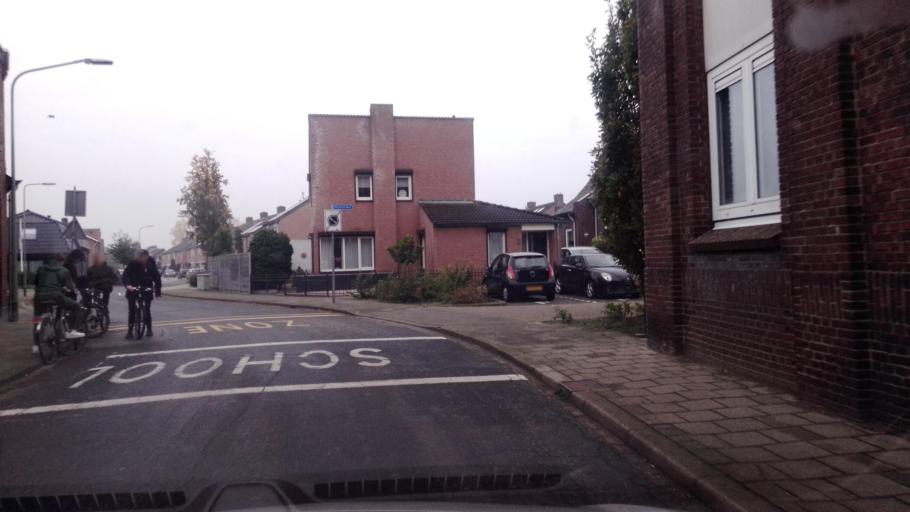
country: NL
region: Limburg
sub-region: Gemeente Peel en Maas
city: Maasbree
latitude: 51.4543
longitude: 6.0500
